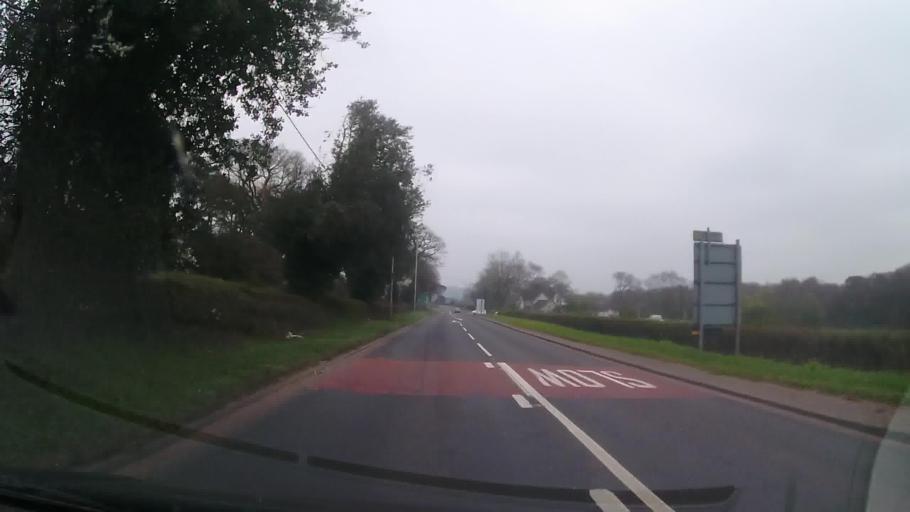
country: GB
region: England
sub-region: Staffordshire
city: Standon
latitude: 52.9463
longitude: -2.3413
